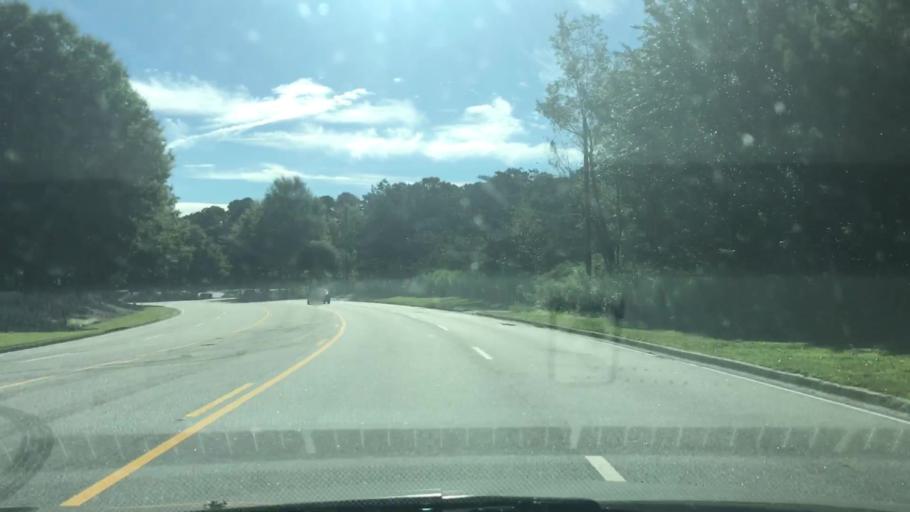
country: US
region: Georgia
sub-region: Gwinnett County
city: Mountain Park
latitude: 33.8143
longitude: -84.1137
